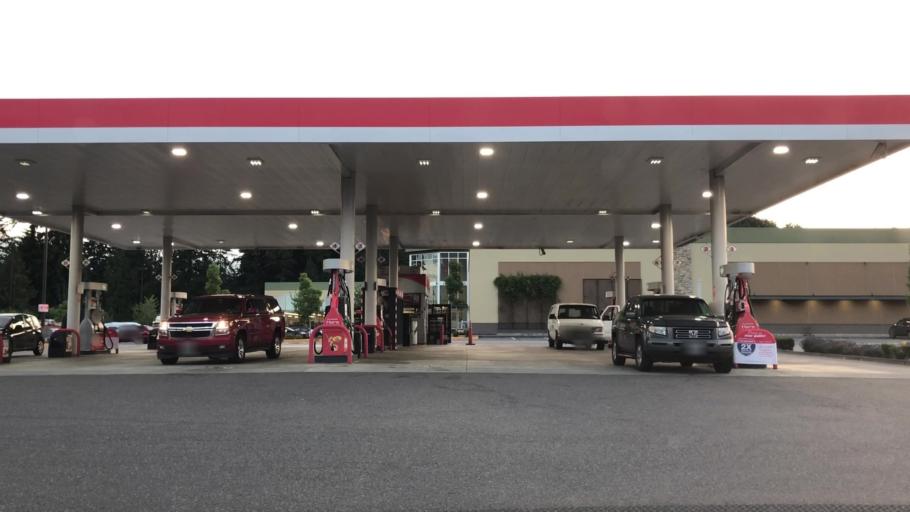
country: US
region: Washington
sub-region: Snohomish County
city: Alderwood Manor
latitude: 47.8471
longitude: -122.2686
